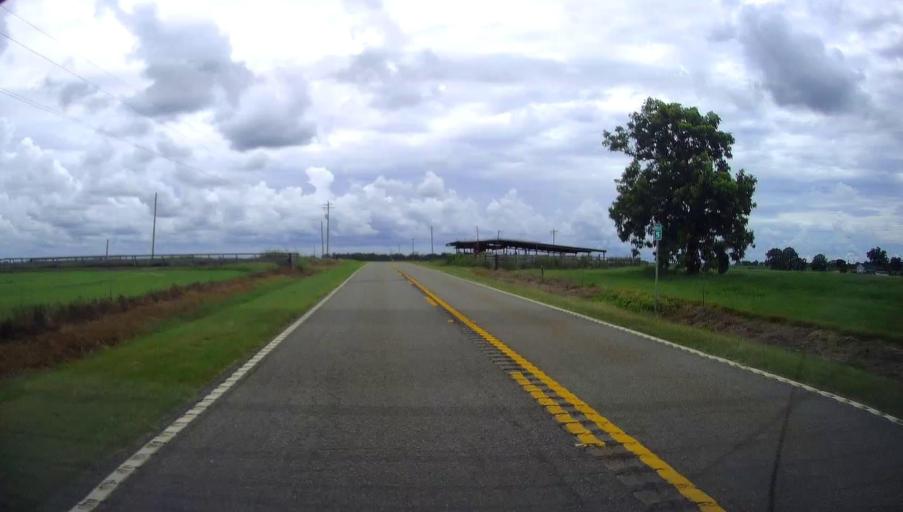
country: US
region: Georgia
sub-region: Dooly County
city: Unadilla
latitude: 32.2707
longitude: -83.8145
